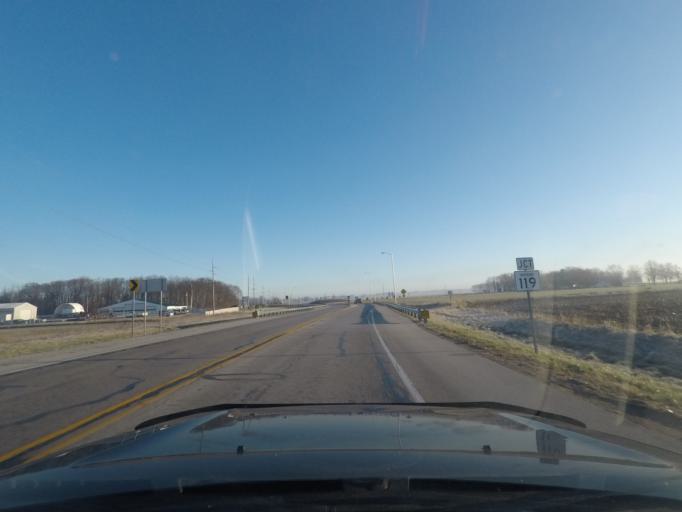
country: US
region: Indiana
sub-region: Elkhart County
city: Wakarusa
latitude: 41.5058
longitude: -86.0020
